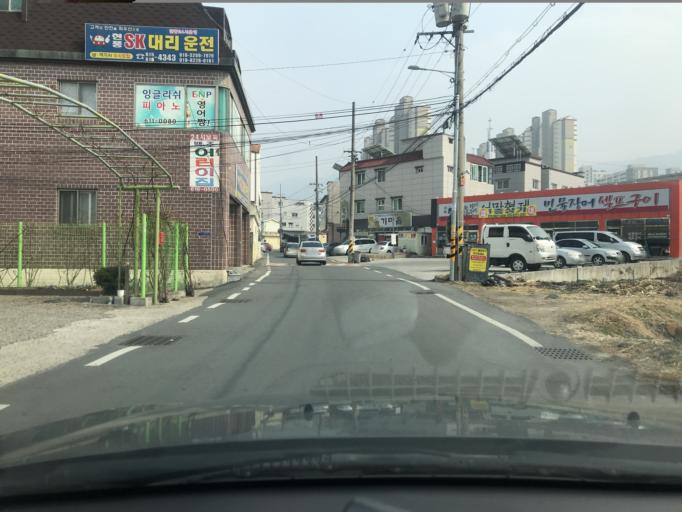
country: KR
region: Daegu
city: Hwawon
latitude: 35.6966
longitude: 128.4517
